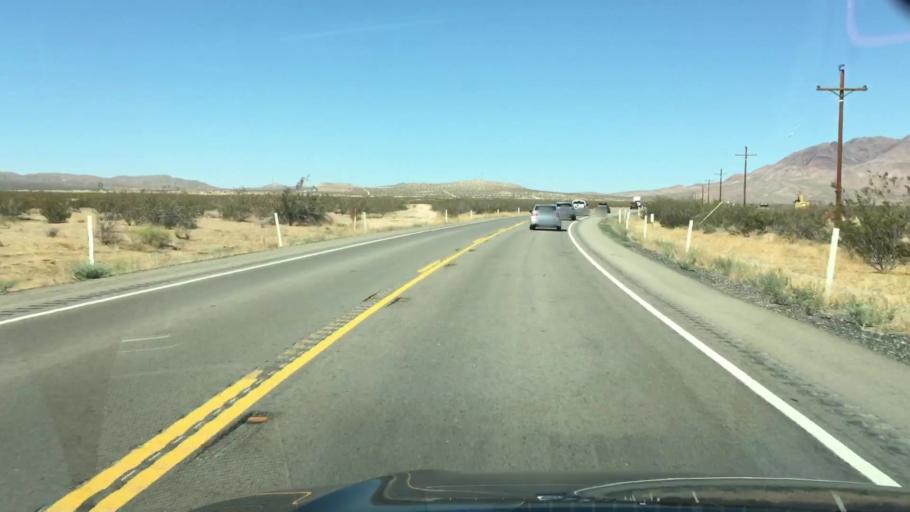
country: US
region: California
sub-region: Kern County
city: Boron
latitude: 35.2865
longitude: -117.6162
